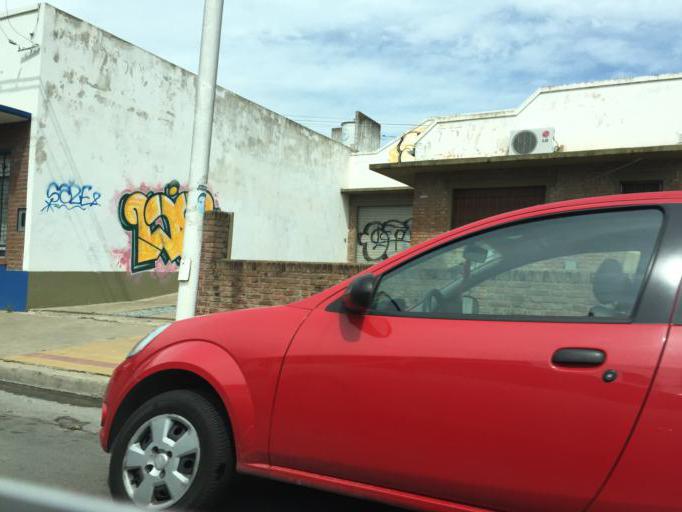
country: AR
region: Buenos Aires
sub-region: Partido de Tandil
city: Tandil
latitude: -37.3263
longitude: -59.1136
